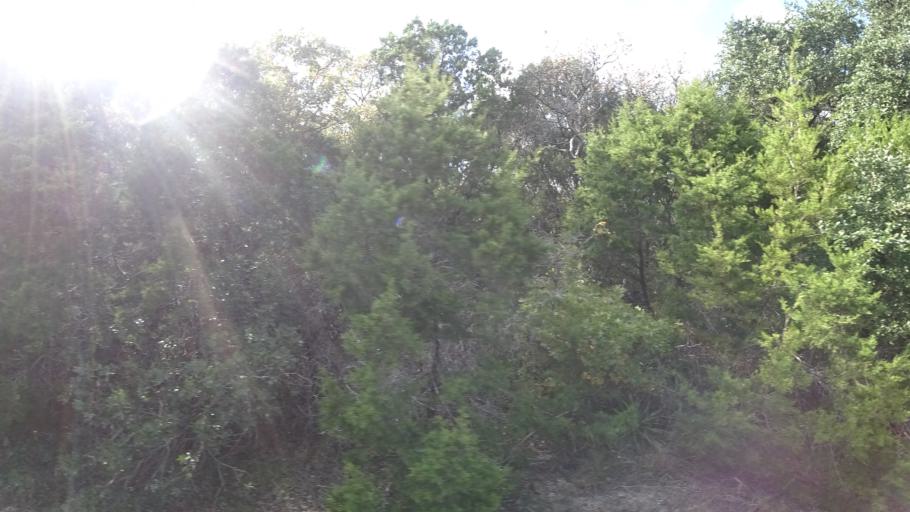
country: US
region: Texas
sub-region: Travis County
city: Barton Creek
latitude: 30.2715
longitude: -97.8841
